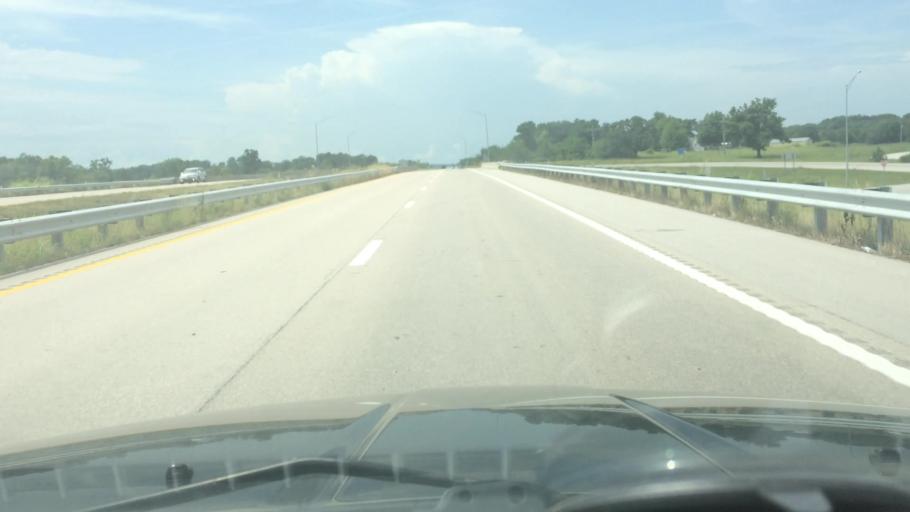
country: US
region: Missouri
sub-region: Polk County
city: Humansville
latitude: 37.7933
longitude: -93.5876
